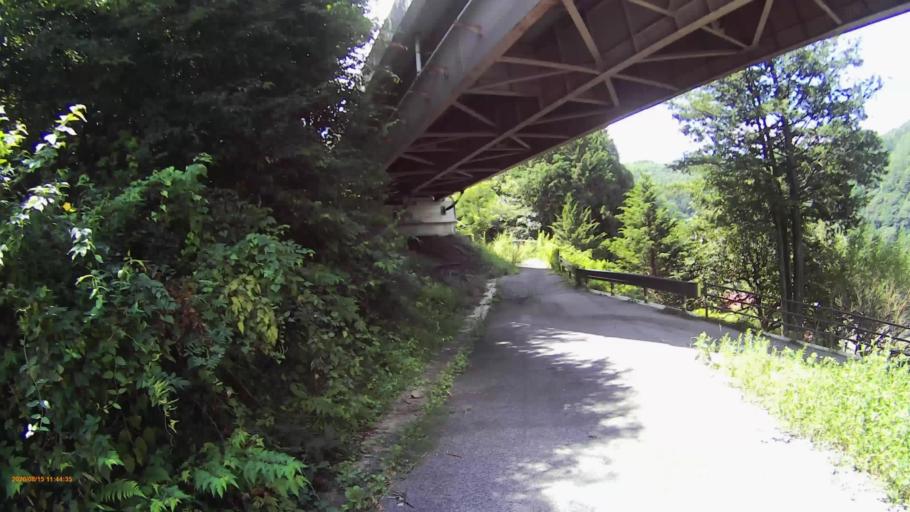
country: JP
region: Nagano
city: Ina
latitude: 35.8313
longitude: 137.6824
